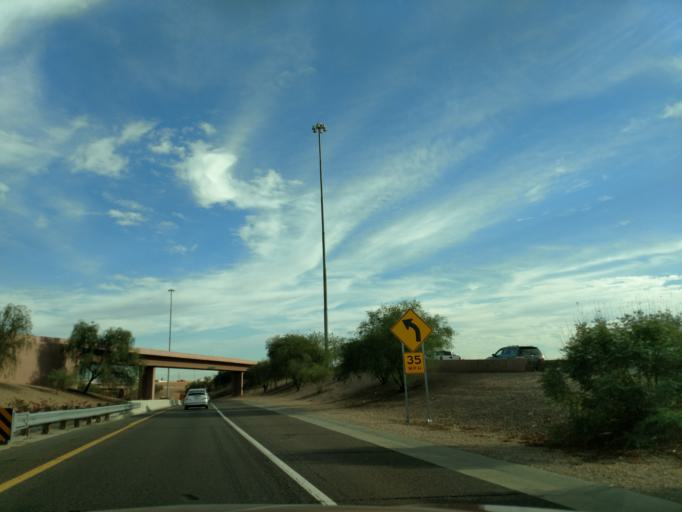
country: US
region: Arizona
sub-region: Maricopa County
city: Tempe
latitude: 33.4336
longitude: -111.8938
